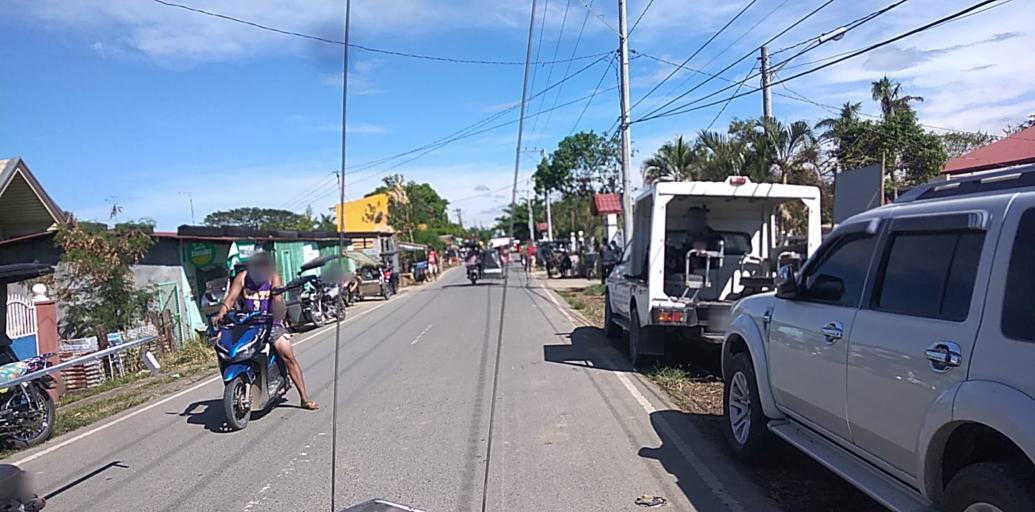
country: PH
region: Central Luzon
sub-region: Province of Pampanga
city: Candaba
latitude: 15.0927
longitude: 120.8122
